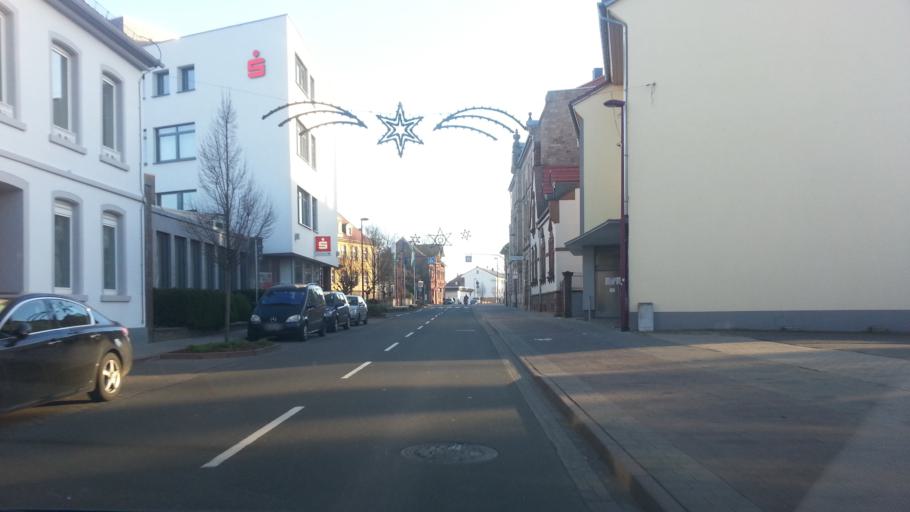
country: DE
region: Rheinland-Pfalz
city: Kirchheimbolanden
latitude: 49.6619
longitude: 8.0140
